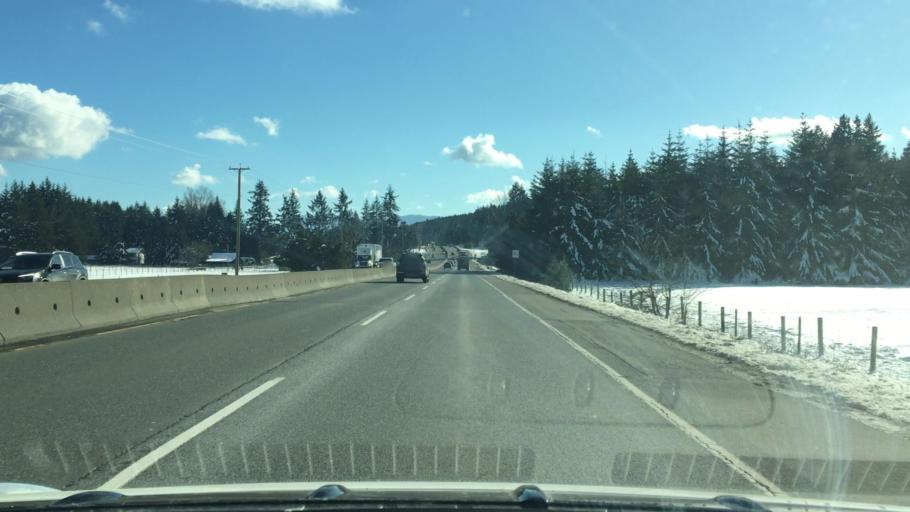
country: CA
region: British Columbia
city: Nanaimo
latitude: 49.0805
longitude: -123.8825
